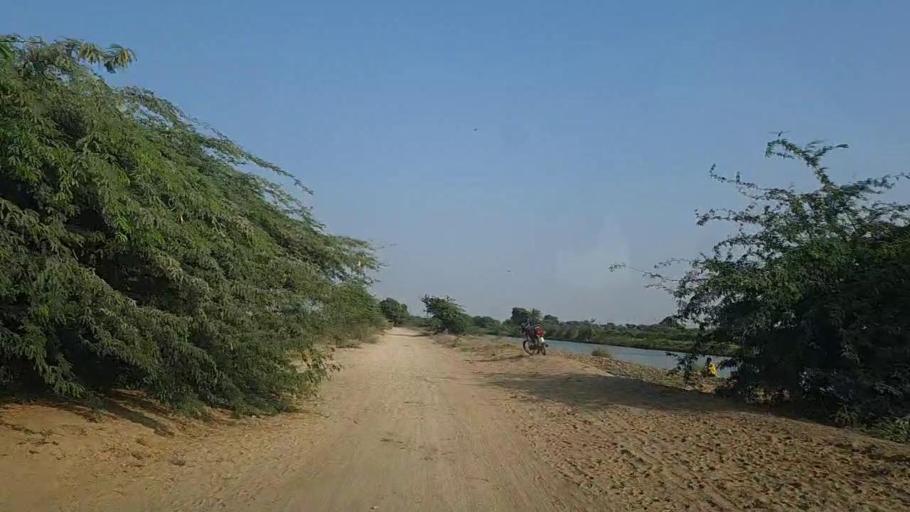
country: PK
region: Sindh
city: Mirpur Sakro
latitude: 24.5747
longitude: 67.6672
